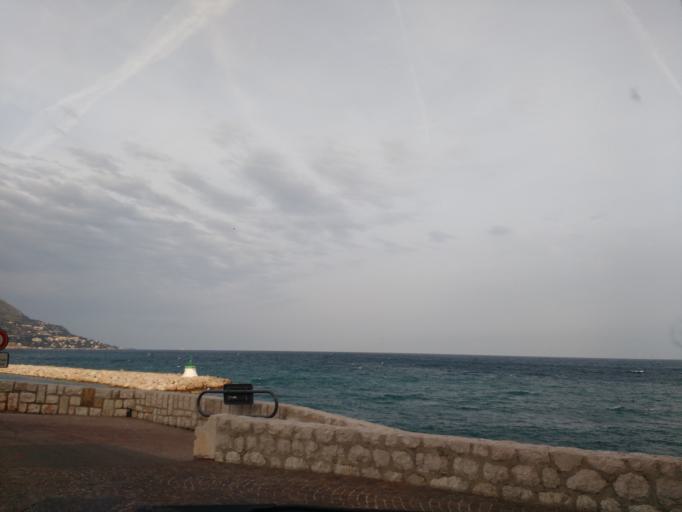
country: FR
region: Provence-Alpes-Cote d'Azur
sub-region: Departement des Alpes-Maritimes
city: Beaulieu-sur-Mer
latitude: 43.7058
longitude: 7.3357
